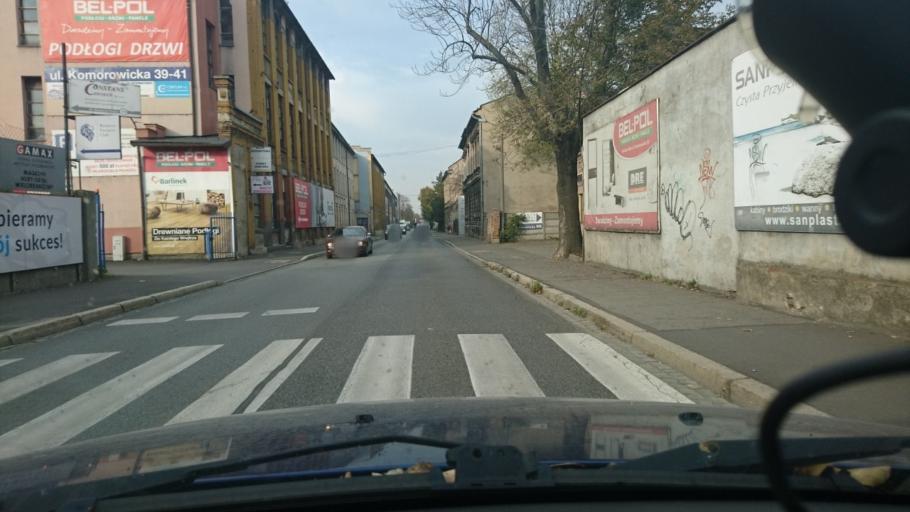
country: PL
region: Silesian Voivodeship
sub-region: Bielsko-Biala
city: Bielsko-Biala
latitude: 49.8293
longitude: 19.0534
